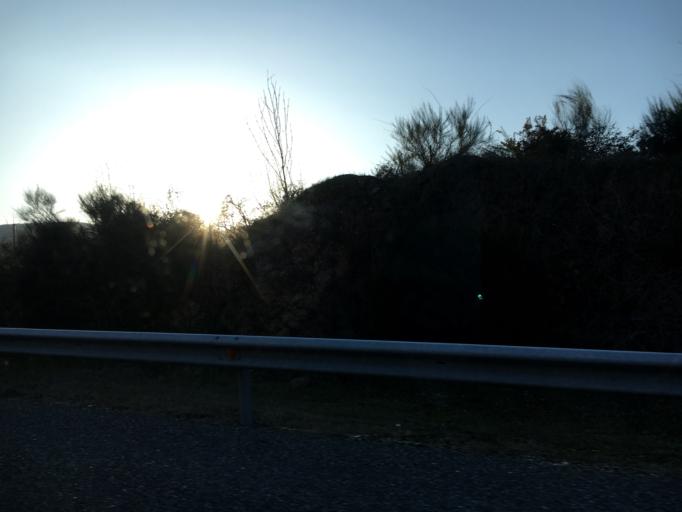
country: ES
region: Galicia
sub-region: Provincia de Lugo
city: Becerrea
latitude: 42.8055
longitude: -7.1063
